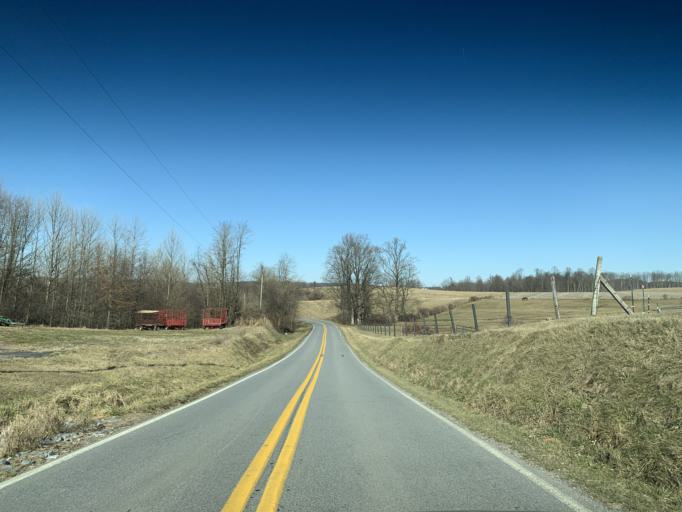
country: US
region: Maryland
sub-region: Carroll County
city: Westminster
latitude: 39.6405
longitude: -76.9656
